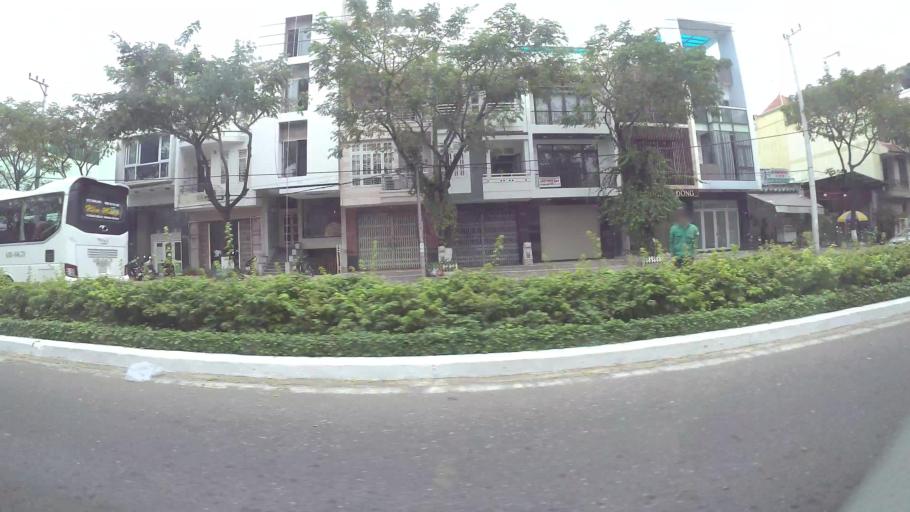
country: VN
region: Da Nang
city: Da Nang
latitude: 16.0863
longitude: 108.2176
